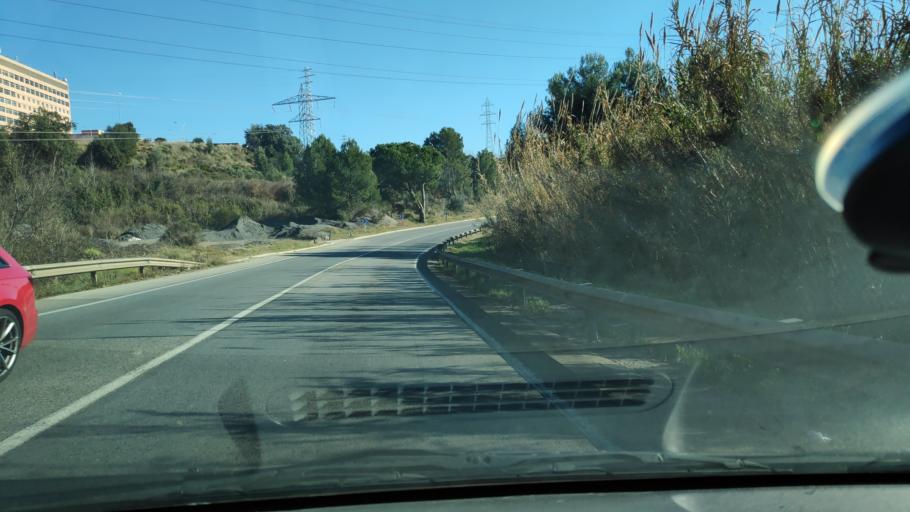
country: ES
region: Catalonia
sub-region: Provincia de Barcelona
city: Terrassa
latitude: 41.5560
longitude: 2.0494
